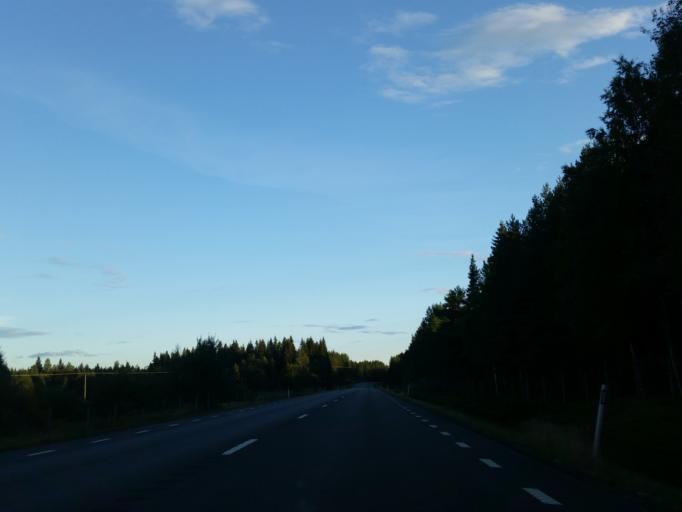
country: SE
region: Vaesterbotten
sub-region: Robertsfors Kommun
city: Robertsfors
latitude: 64.0298
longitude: 20.8415
